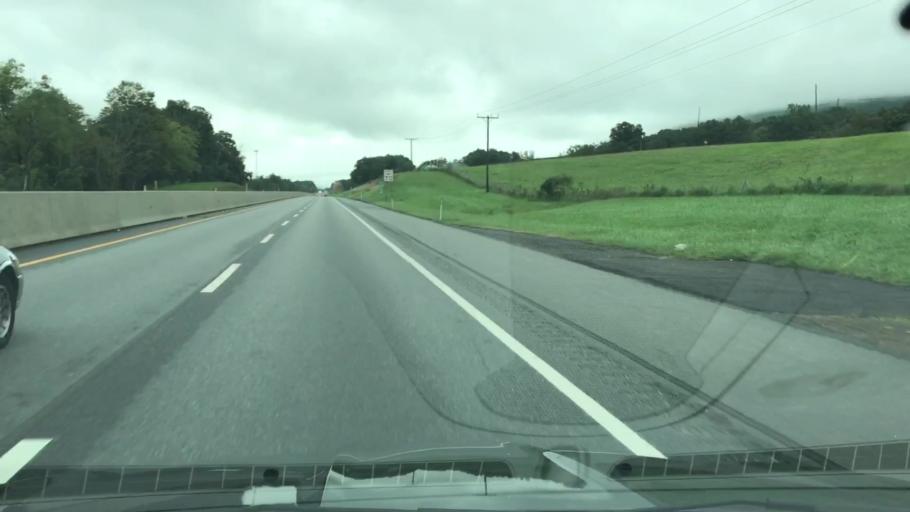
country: US
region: Pennsylvania
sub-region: Franklin County
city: Doylestown
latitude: 40.1374
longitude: -77.7332
